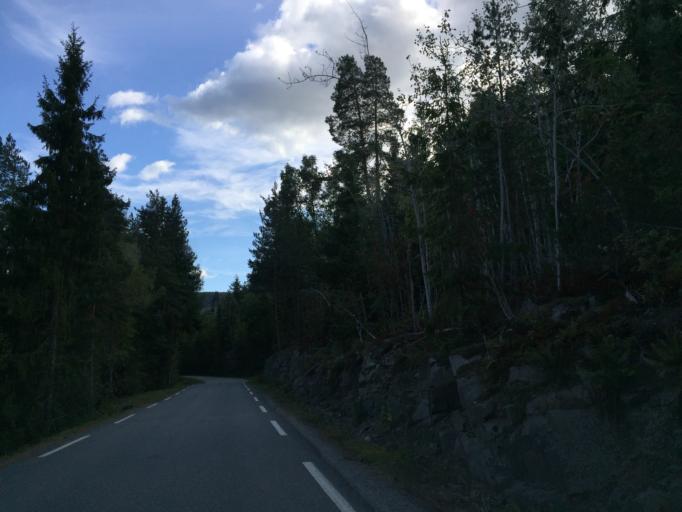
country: NO
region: Buskerud
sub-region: Ovre Eiker
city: Hokksund
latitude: 59.6476
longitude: 9.9204
